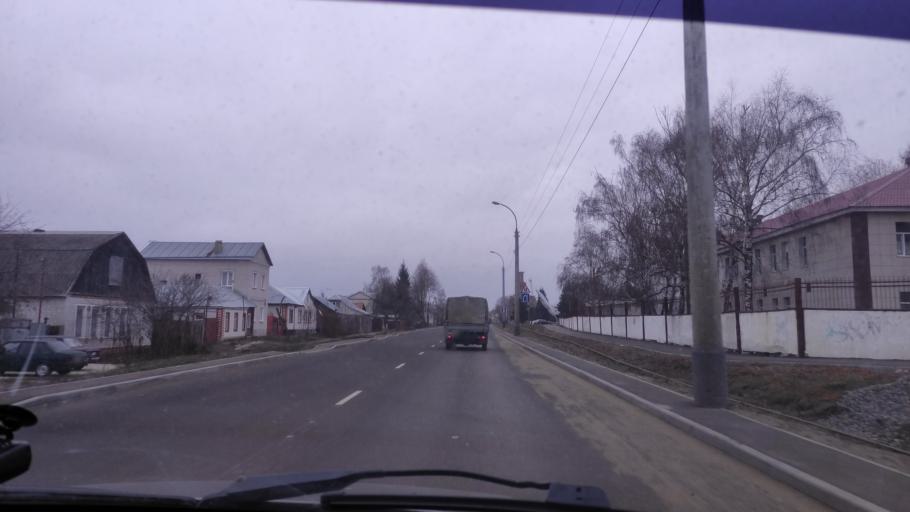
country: RU
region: Tambov
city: Tambov
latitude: 52.7216
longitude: 41.4186
